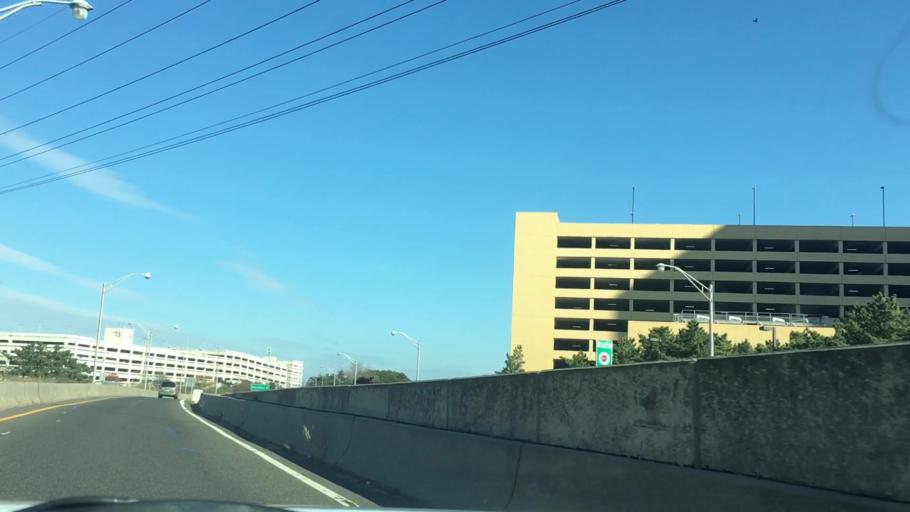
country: US
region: New Jersey
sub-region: Atlantic County
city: Atlantic City
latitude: 39.3806
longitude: -74.4291
